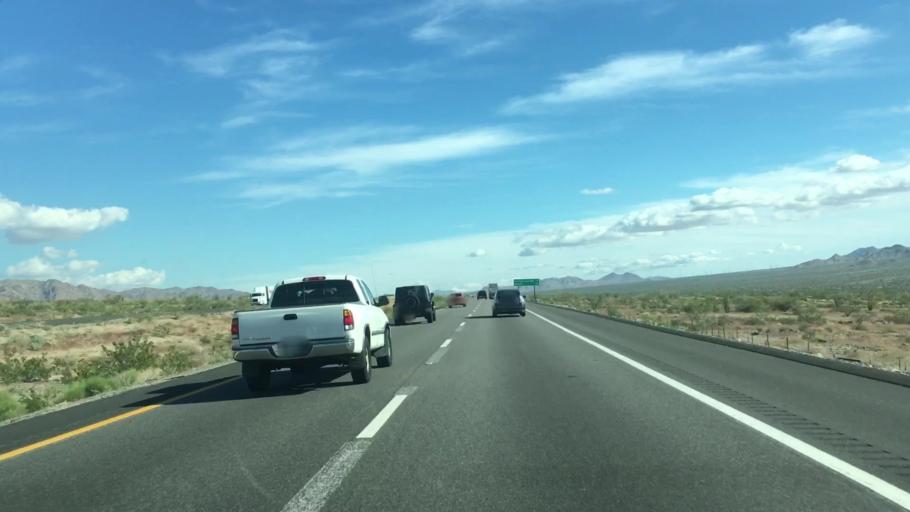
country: US
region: California
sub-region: Riverside County
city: Mecca
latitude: 33.6642
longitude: -115.8731
